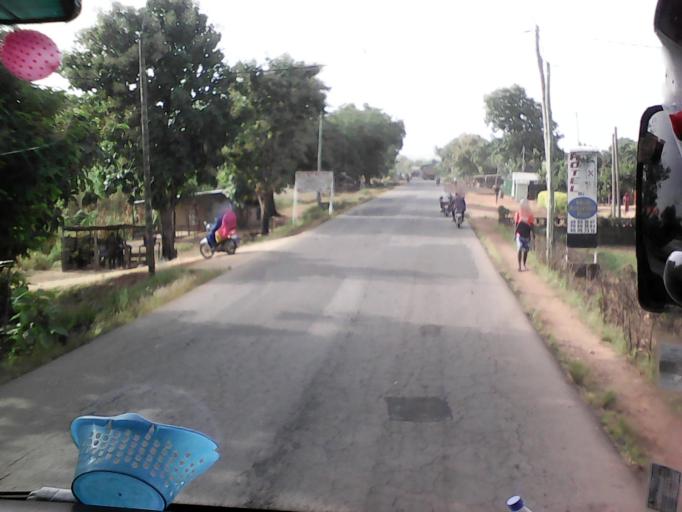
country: TG
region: Kara
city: Kara
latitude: 9.5115
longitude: 1.2089
